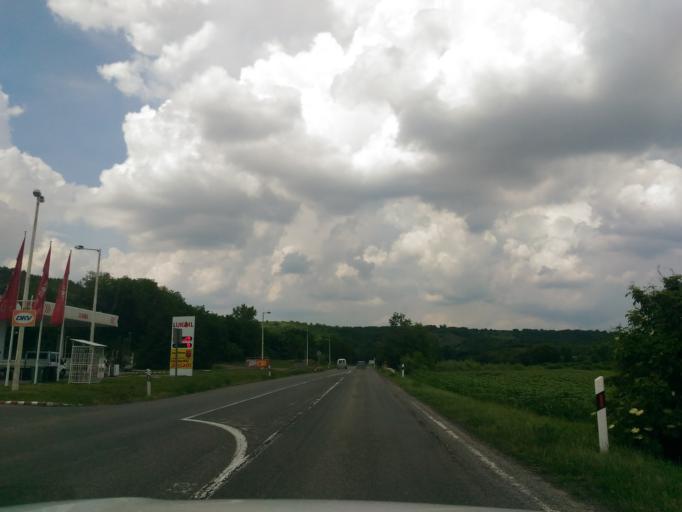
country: HU
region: Baranya
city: Mecseknadasd
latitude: 46.2402
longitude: 18.4795
